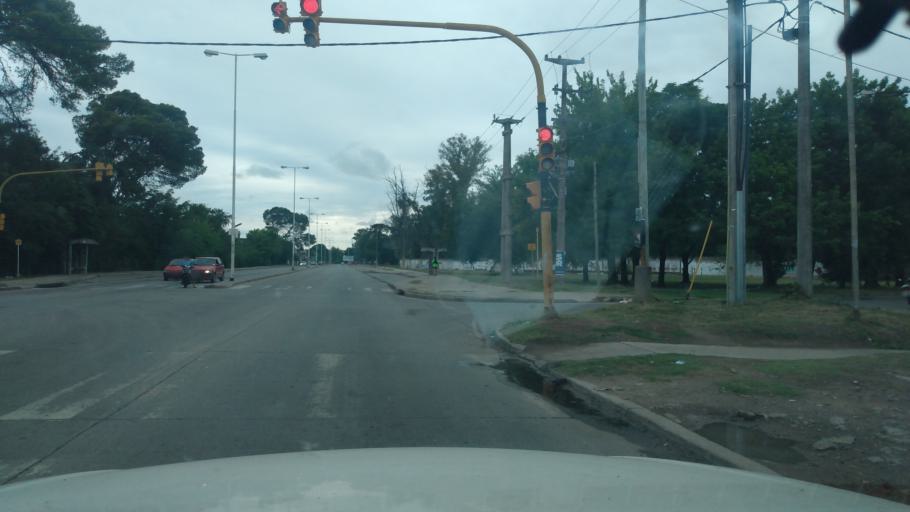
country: AR
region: Buenos Aires
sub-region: Partido de Lujan
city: Lujan
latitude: -34.5566
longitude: -59.1161
